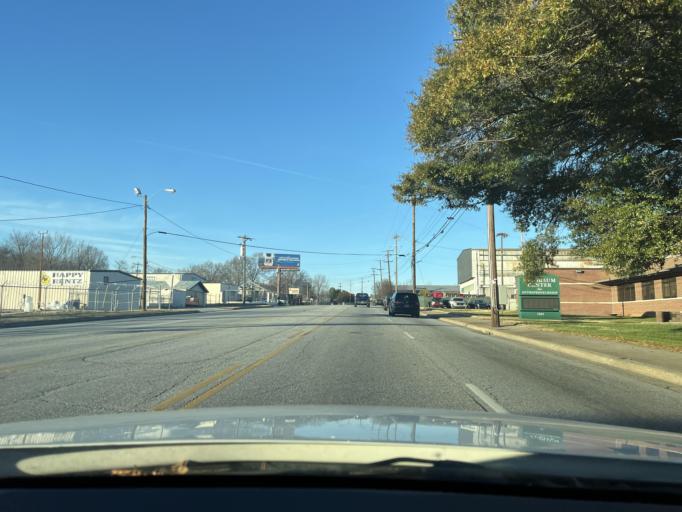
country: US
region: North Carolina
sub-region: Guilford County
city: Greensboro
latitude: 36.0499
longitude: -79.7914
